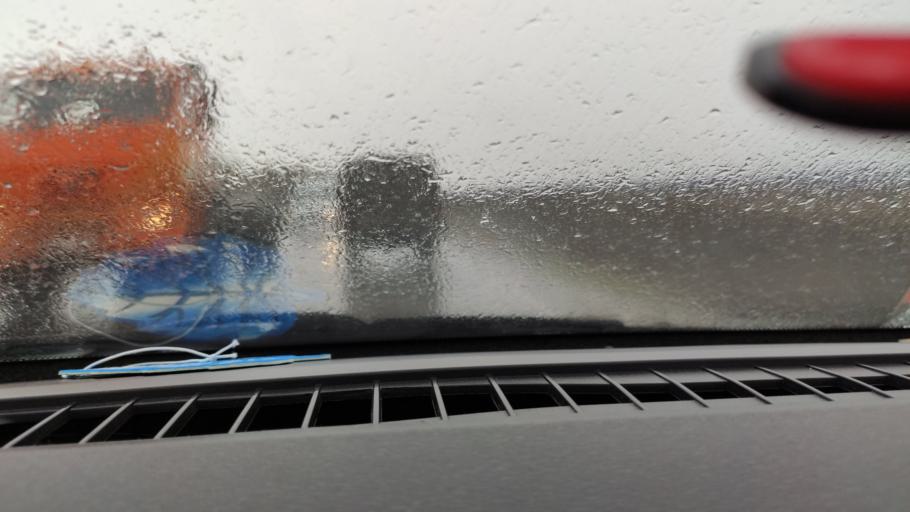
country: RU
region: Tatarstan
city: Nurlat
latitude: 54.6264
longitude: 50.9451
